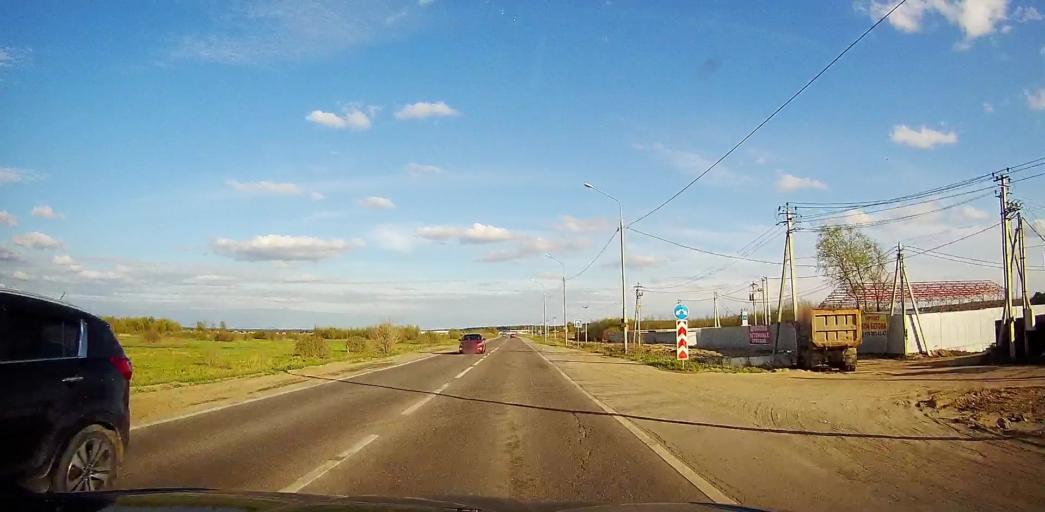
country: RU
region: Moskovskaya
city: Malyshevo
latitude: 55.4935
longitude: 38.3122
